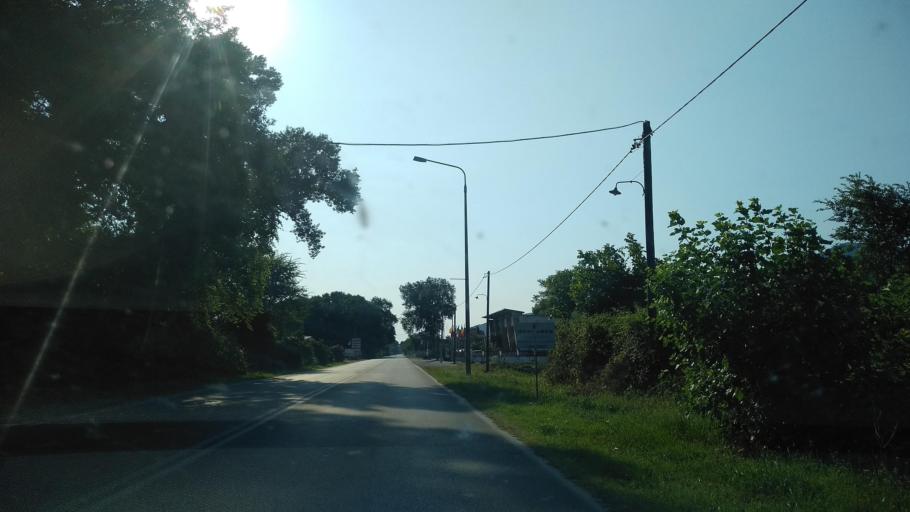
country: GR
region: Central Macedonia
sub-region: Nomos Thessalonikis
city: Stavros
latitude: 40.6698
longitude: 23.6675
